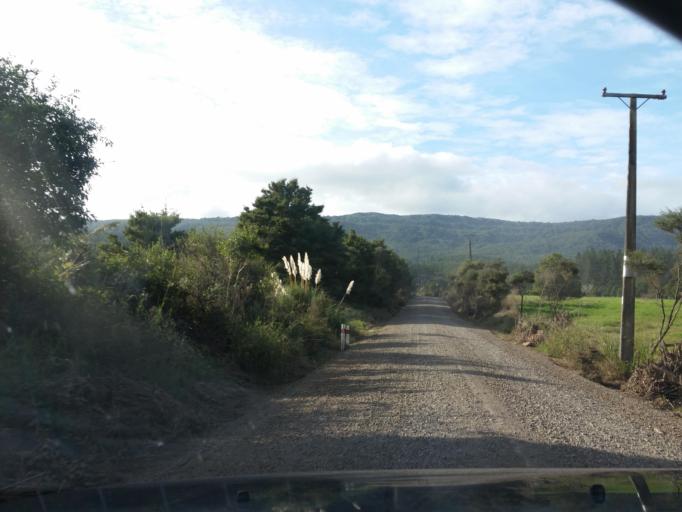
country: NZ
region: Northland
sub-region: Kaipara District
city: Dargaville
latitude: -35.7766
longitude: 173.7138
